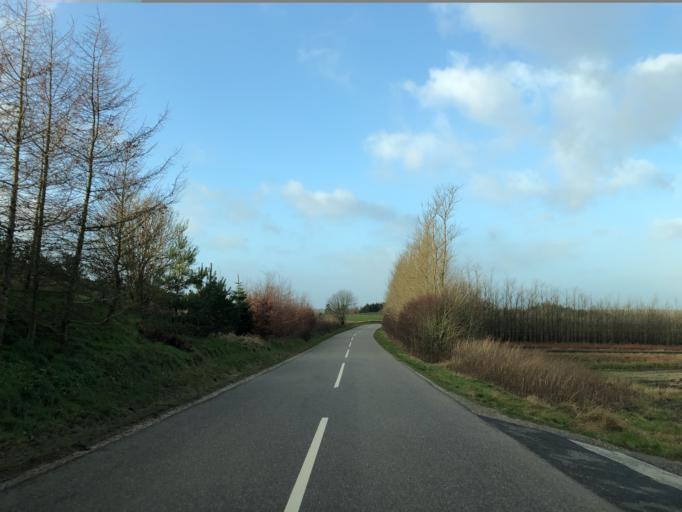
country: DK
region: Central Jutland
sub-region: Ringkobing-Skjern Kommune
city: Videbaek
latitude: 56.1897
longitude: 8.5442
